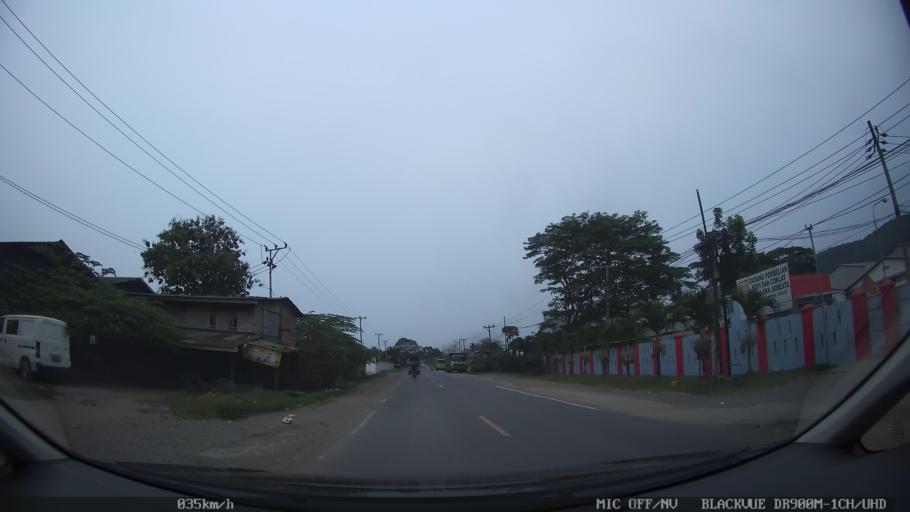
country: ID
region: Lampung
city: Panjang
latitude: -5.4281
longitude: 105.3281
